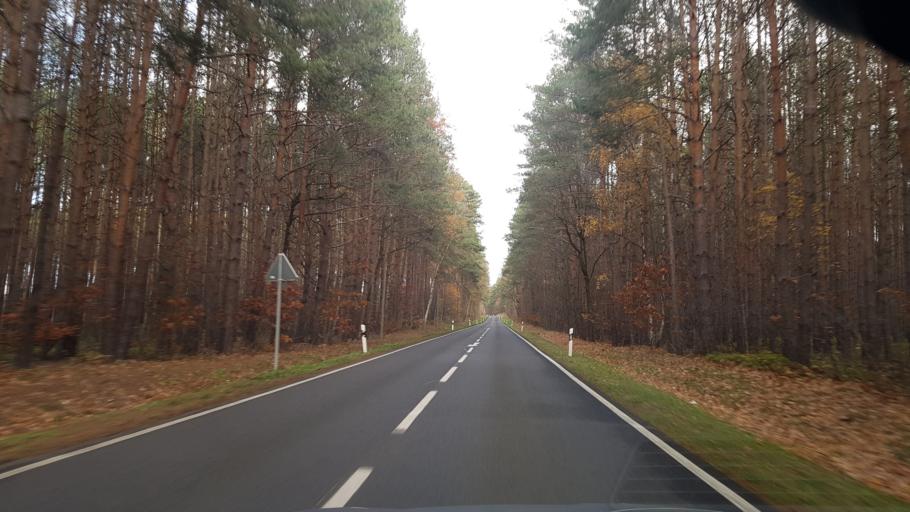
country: DE
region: Brandenburg
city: Sonnewalde
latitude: 51.7205
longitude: 13.6859
